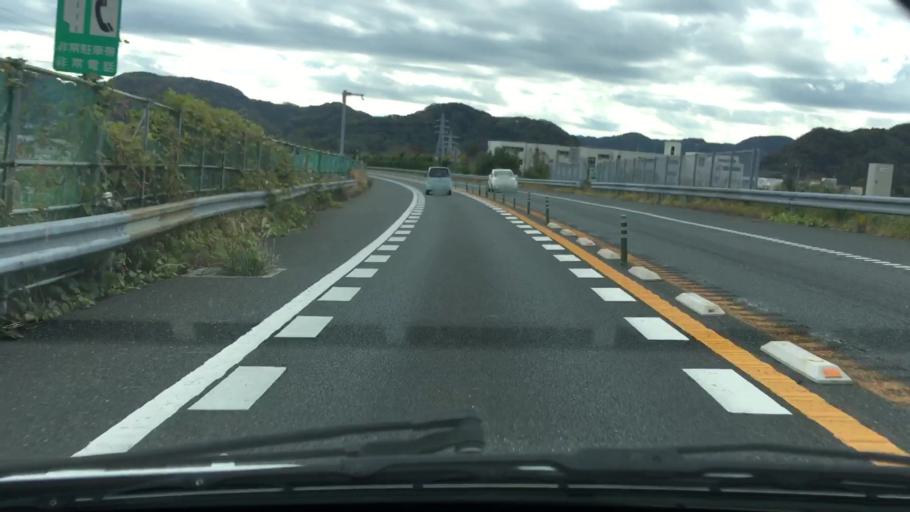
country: JP
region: Chiba
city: Kimitsu
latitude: 35.2222
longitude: 139.8845
